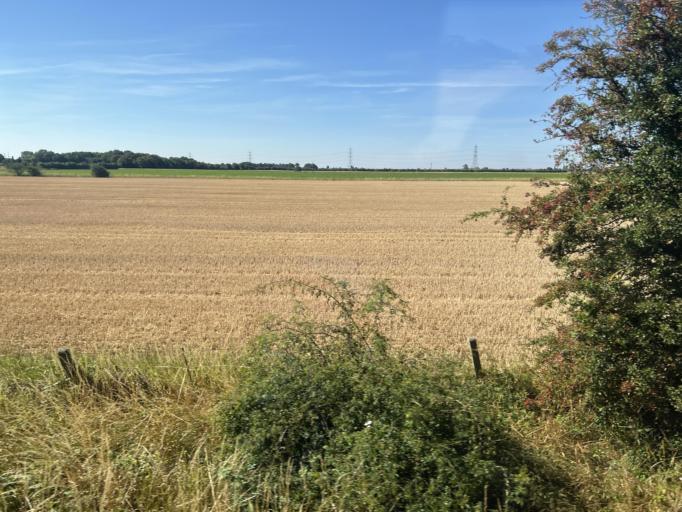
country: GB
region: England
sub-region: Lincolnshire
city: Heckington
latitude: 52.9694
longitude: -0.2507
